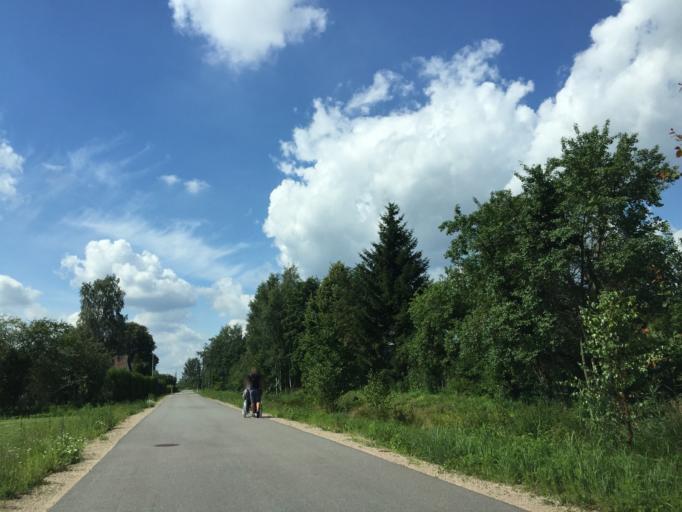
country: LV
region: Olaine
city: Olaine
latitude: 56.8055
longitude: 23.9878
